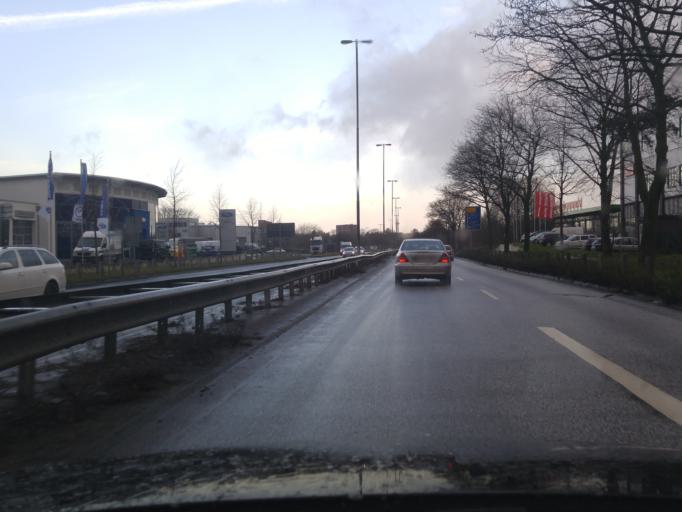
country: DE
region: Schleswig-Holstein
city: Luebeck
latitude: 53.8775
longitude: 10.6673
